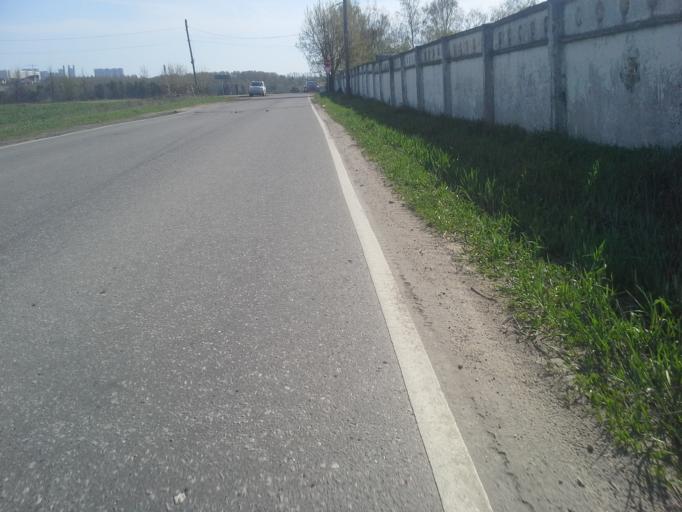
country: RU
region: Moskovskaya
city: Dubrovitsy
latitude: 55.4423
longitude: 37.4758
